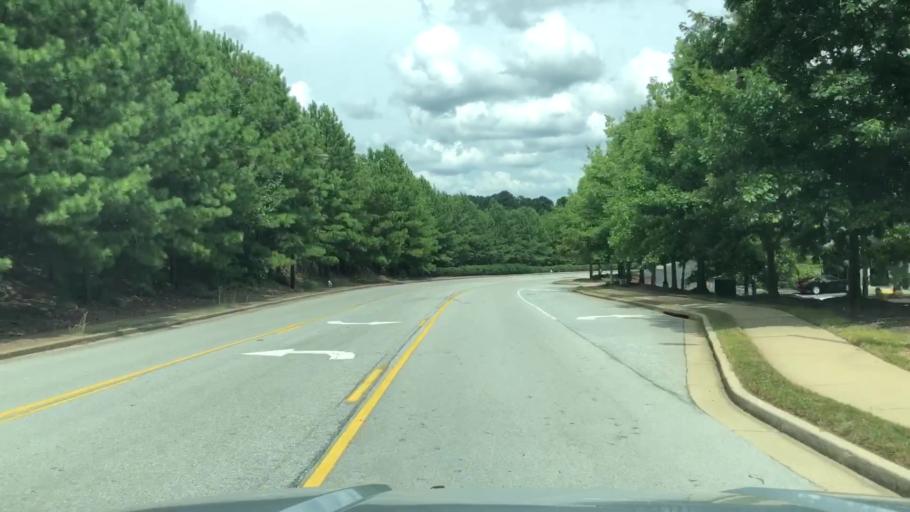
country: US
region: Georgia
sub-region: Gwinnett County
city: Suwanee
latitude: 34.0388
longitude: -84.0315
